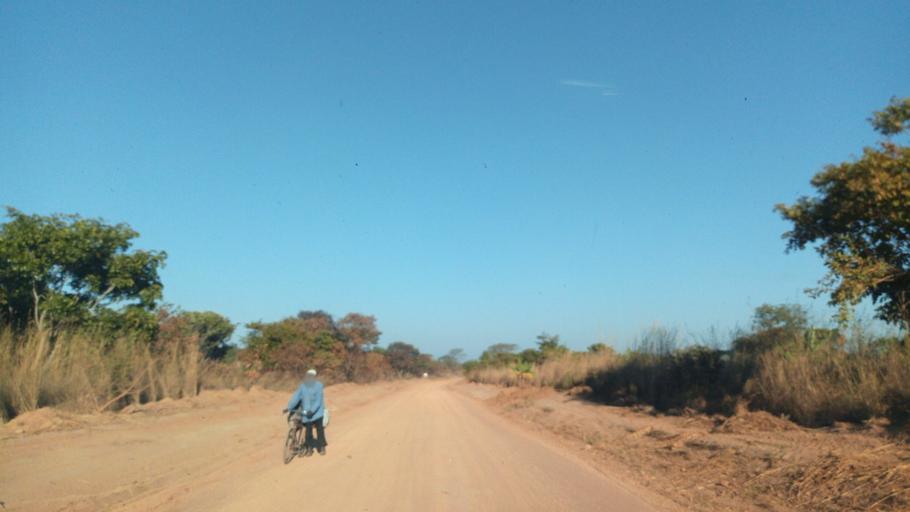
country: ZM
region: Luapula
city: Mwense
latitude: -10.4476
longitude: 28.5620
